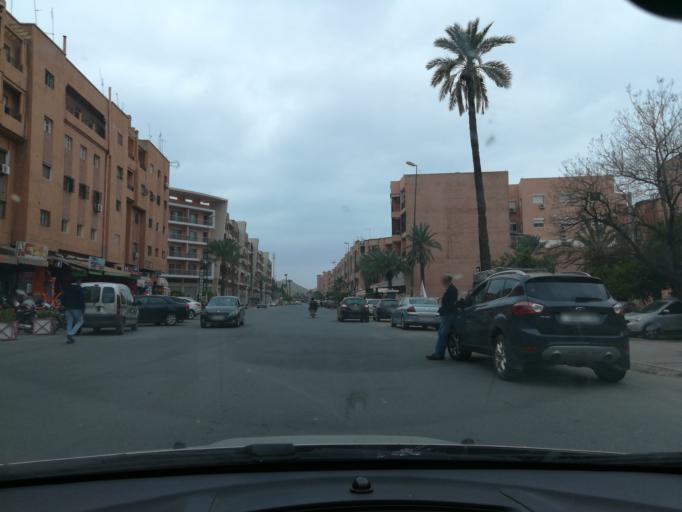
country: MA
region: Marrakech-Tensift-Al Haouz
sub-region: Marrakech
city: Marrakesh
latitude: 31.6489
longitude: -8.0085
